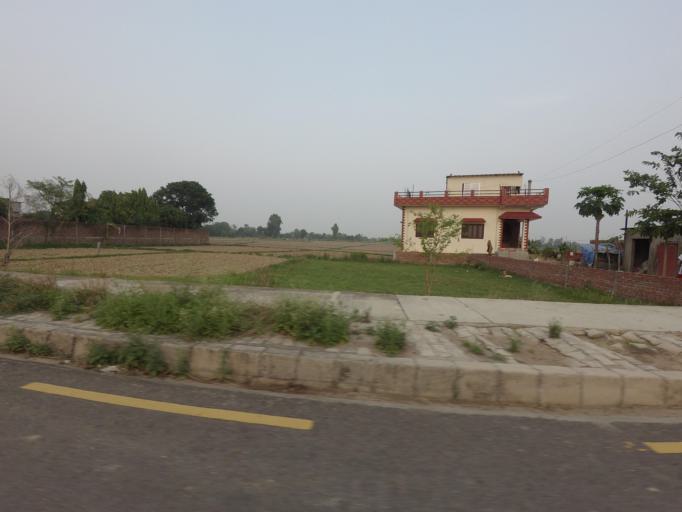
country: NP
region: Western Region
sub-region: Lumbini Zone
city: Bhairahawa
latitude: 27.4994
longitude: 83.4627
